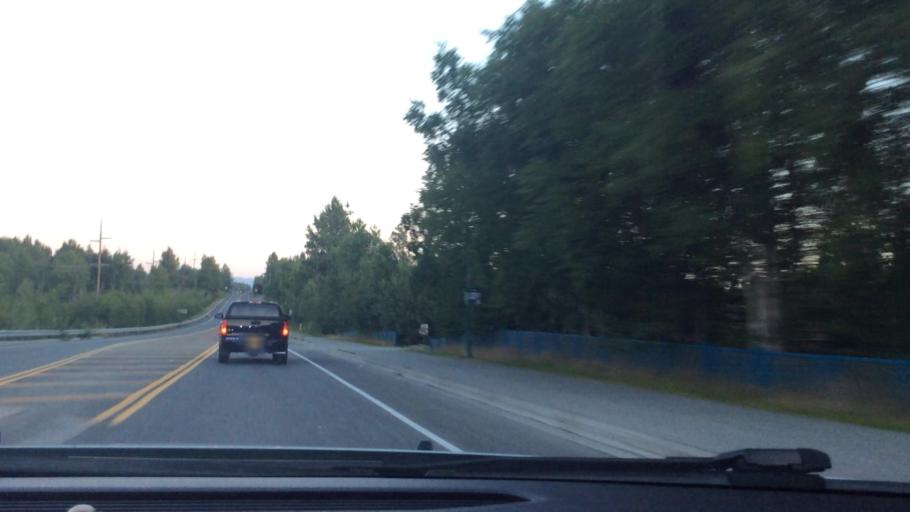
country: US
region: Alaska
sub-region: Anchorage Municipality
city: Anchorage
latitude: 61.1516
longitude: -149.8043
